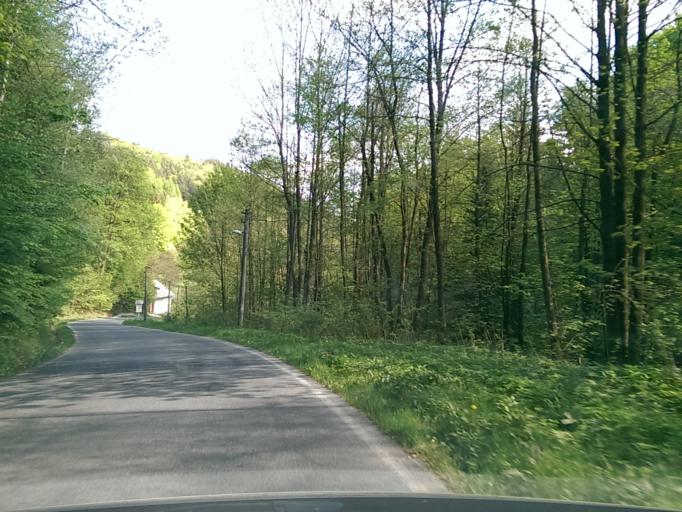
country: CZ
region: Liberecky
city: Mala Skala
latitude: 50.6562
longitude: 15.2180
